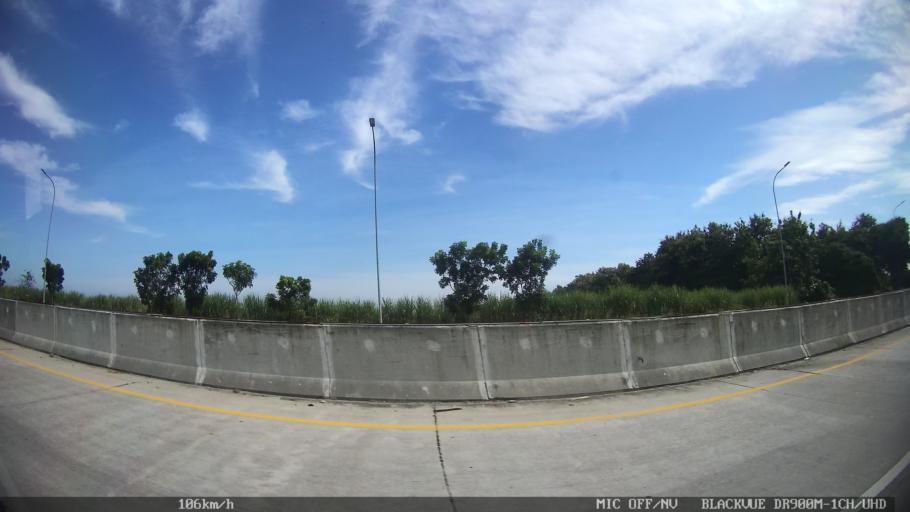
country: ID
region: North Sumatra
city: Medan
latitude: 3.6378
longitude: 98.6335
